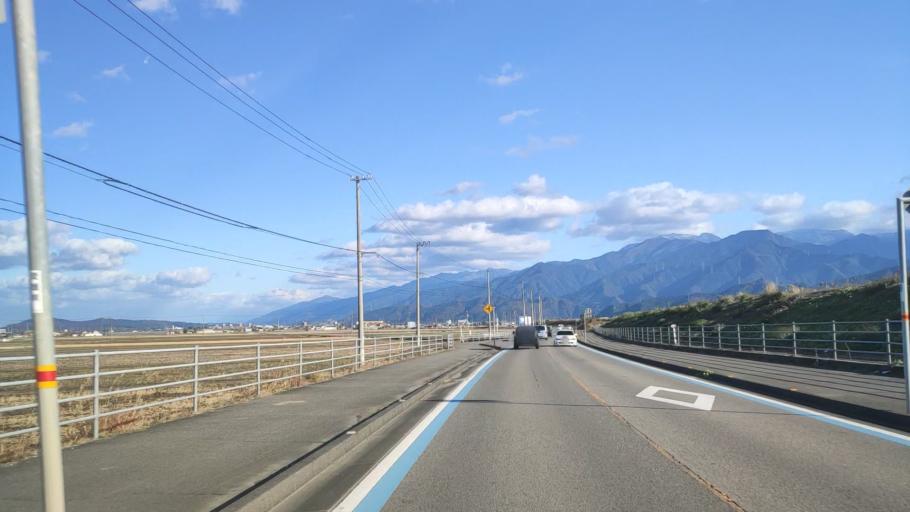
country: JP
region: Ehime
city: Saijo
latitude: 33.9105
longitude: 133.1344
